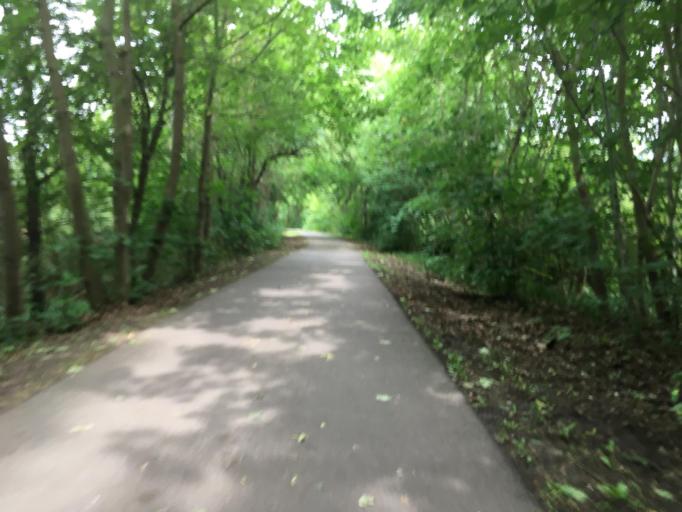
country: DE
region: Brandenburg
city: Prenzlau
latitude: 53.3028
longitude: 13.8460
